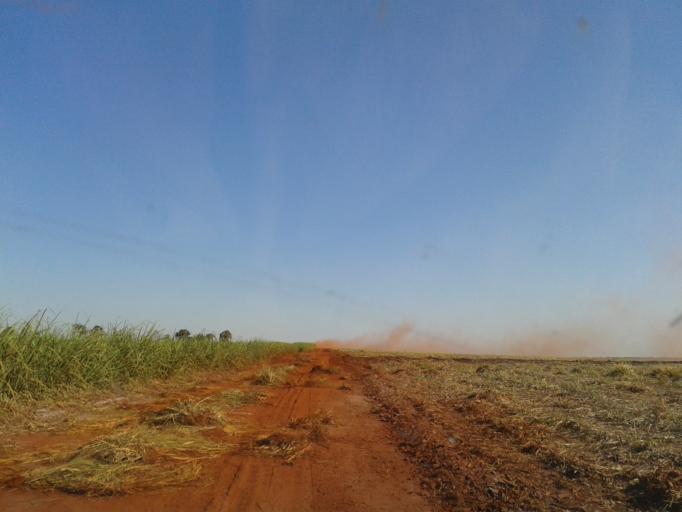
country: BR
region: Minas Gerais
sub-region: Santa Vitoria
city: Santa Vitoria
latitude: -18.7350
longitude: -50.2592
